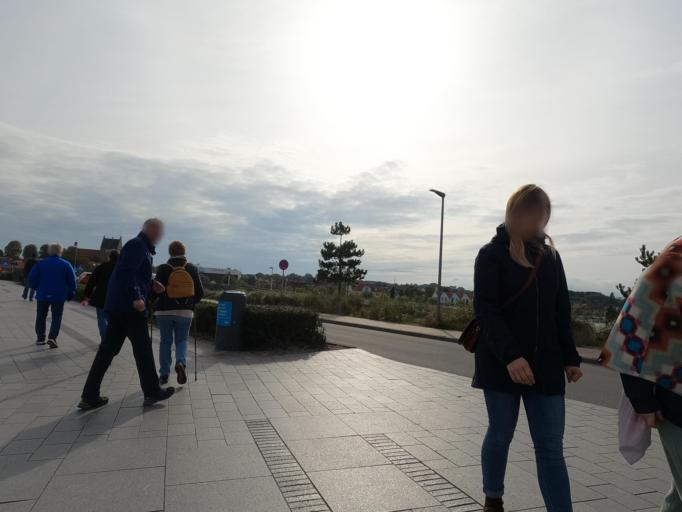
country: DE
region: Schleswig-Holstein
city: Heiligenhafen
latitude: 54.3762
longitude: 10.9799
